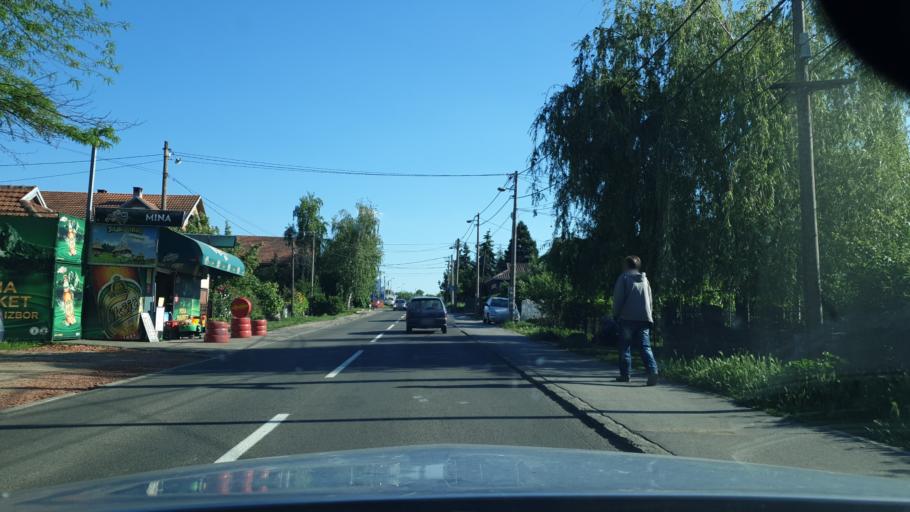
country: RS
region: Central Serbia
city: Sremcica
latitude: 44.7134
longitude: 20.3681
